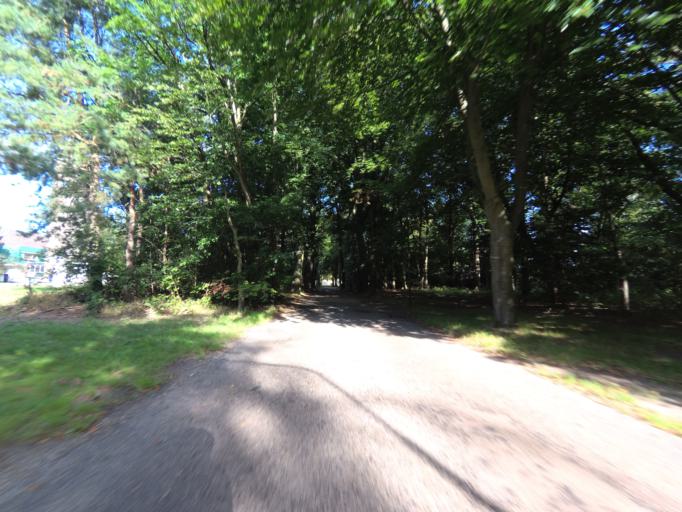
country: NL
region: Utrecht
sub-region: Gemeente Utrechtse Heuvelrug
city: Maarsbergen
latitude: 52.0402
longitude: 5.4196
